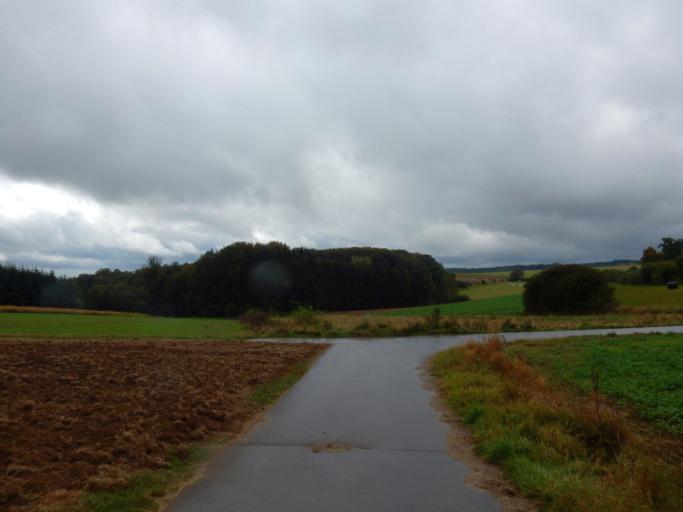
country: LU
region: Luxembourg
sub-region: Canton de Capellen
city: Kehlen
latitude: 49.6886
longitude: 6.0174
